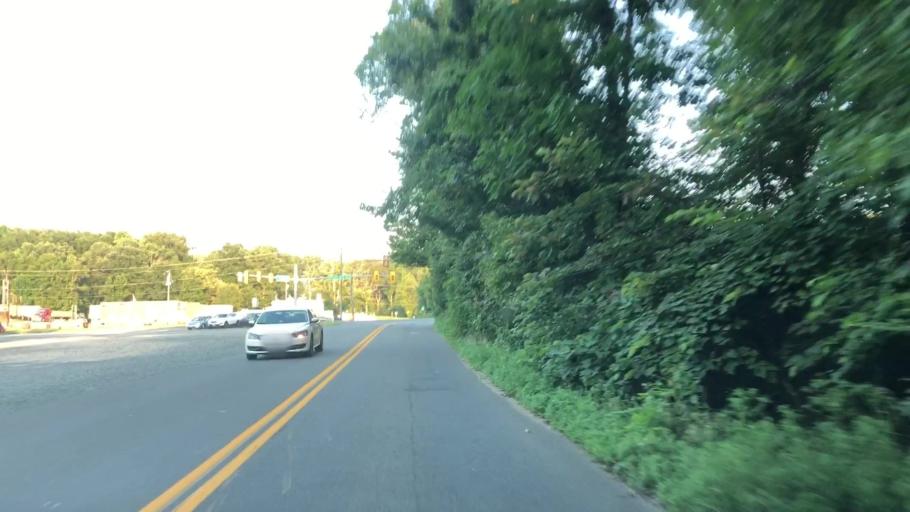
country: US
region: Virginia
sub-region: Stafford County
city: Stafford
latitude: 38.3960
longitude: -77.4307
